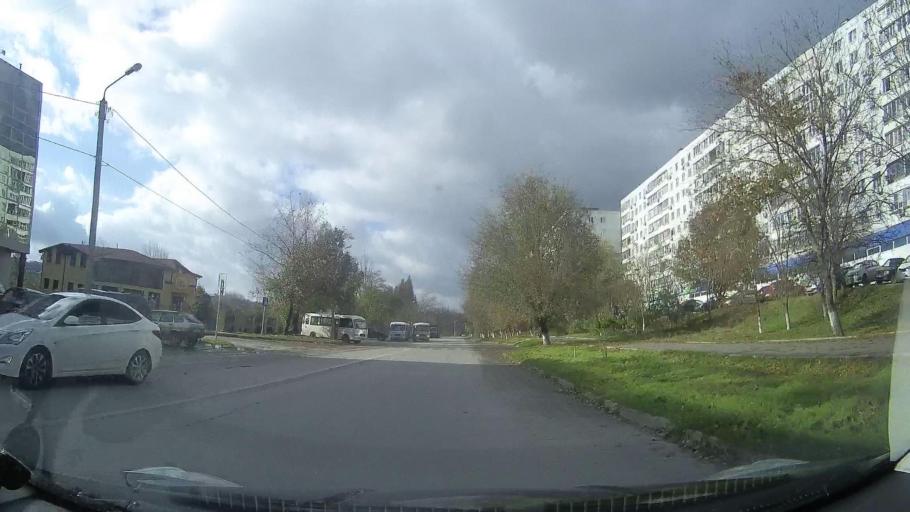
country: RU
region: Rostov
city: Severnyy
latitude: 47.2889
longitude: 39.6937
